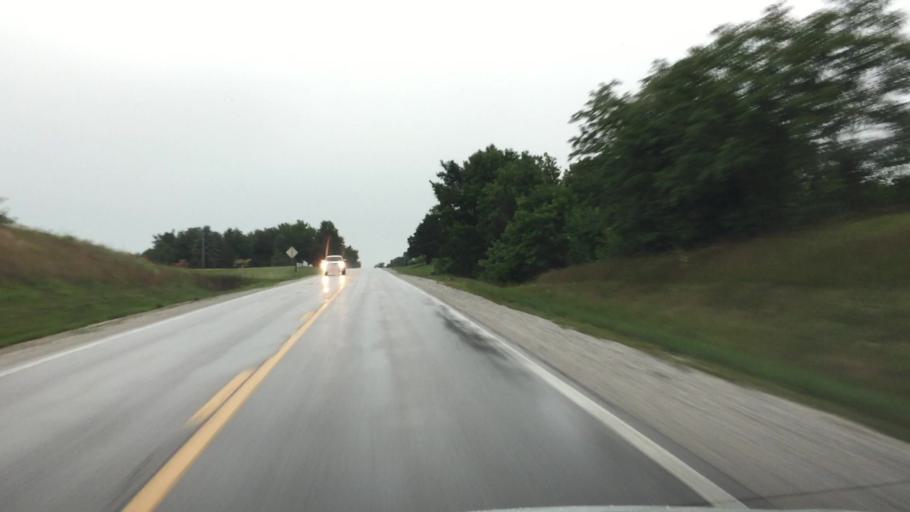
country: US
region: Illinois
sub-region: Hancock County
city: Carthage
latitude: 40.4327
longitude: -91.1401
